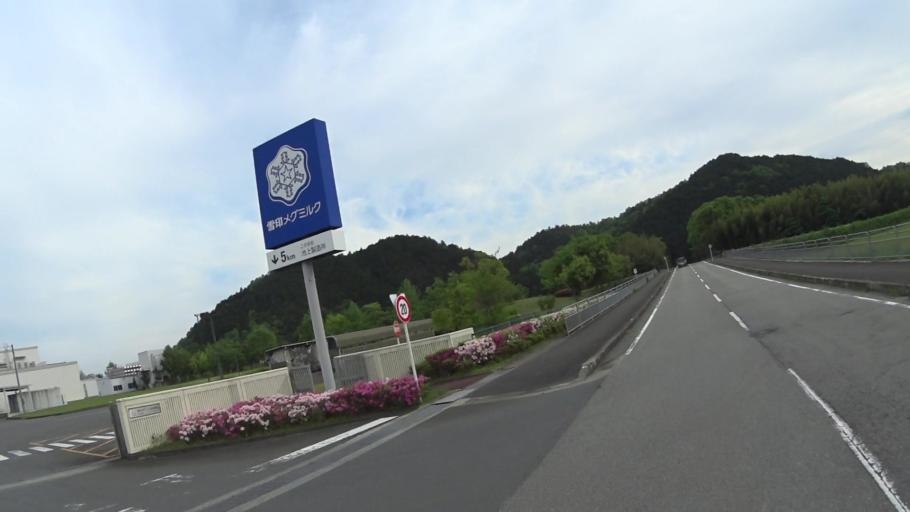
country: JP
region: Kyoto
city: Kameoka
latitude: 35.0956
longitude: 135.5063
